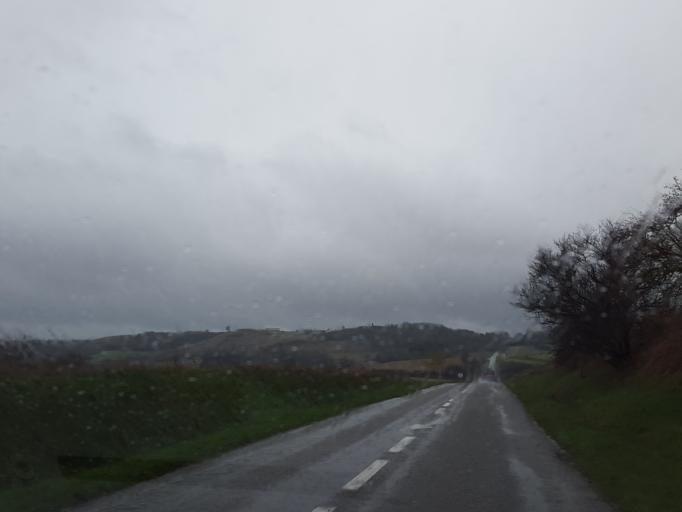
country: FR
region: Languedoc-Roussillon
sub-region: Departement de l'Aude
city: Bram
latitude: 43.1910
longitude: 2.0511
